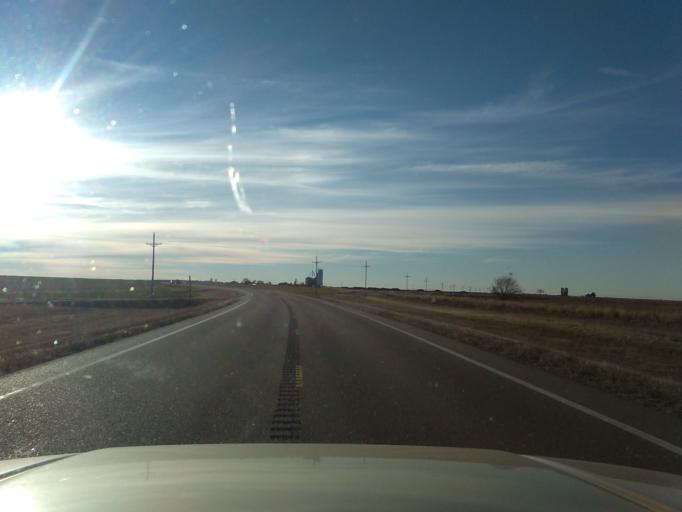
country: US
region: Kansas
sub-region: Thomas County
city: Colby
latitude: 39.4531
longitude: -100.8009
